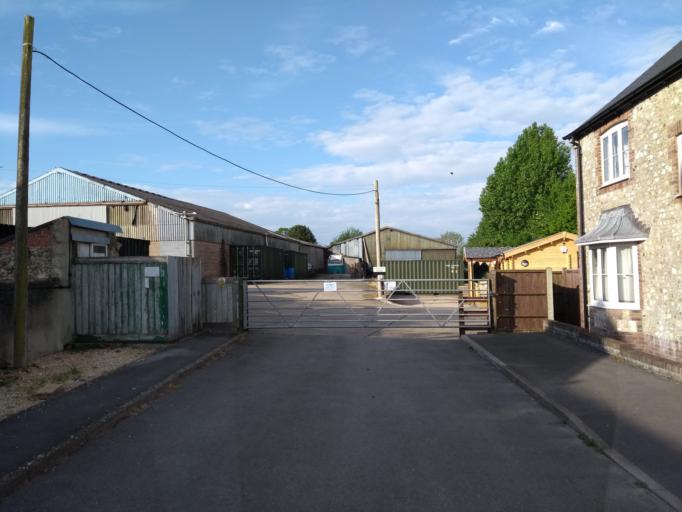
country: GB
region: England
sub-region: Devon
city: Axminster
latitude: 50.7999
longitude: -2.9349
